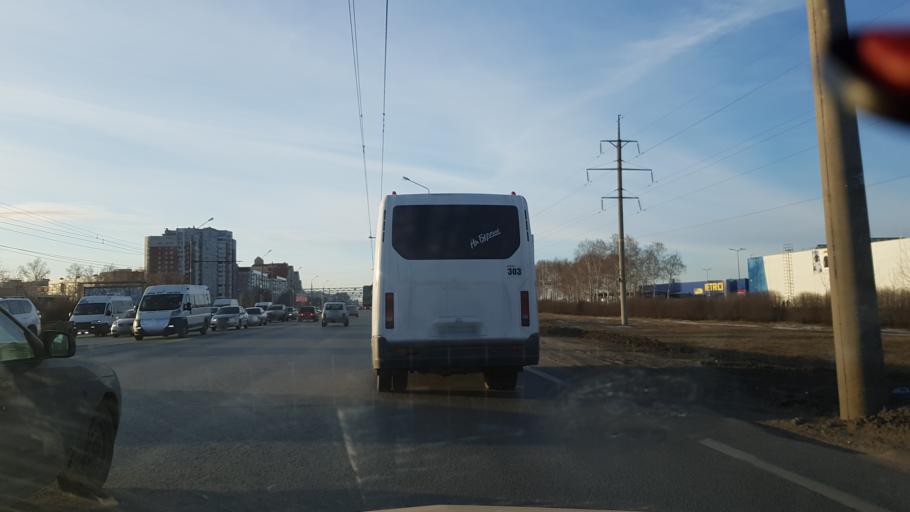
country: RU
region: Samara
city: Tol'yatti
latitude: 53.5455
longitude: 49.3780
